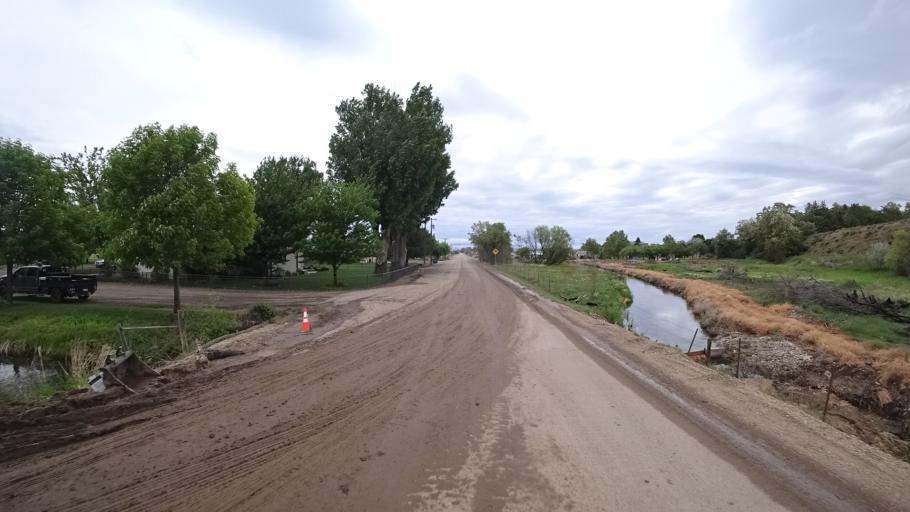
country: US
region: Idaho
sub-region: Ada County
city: Star
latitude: 43.6704
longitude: -116.5050
